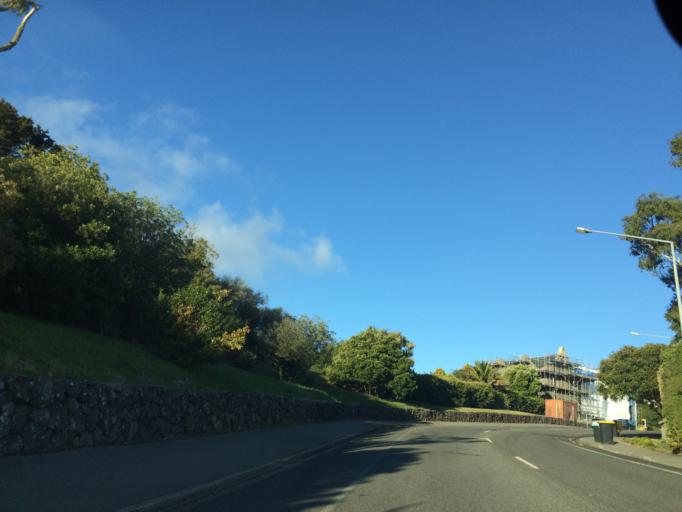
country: NZ
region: Canterbury
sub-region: Christchurch City
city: Christchurch
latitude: -43.5812
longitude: 172.6338
